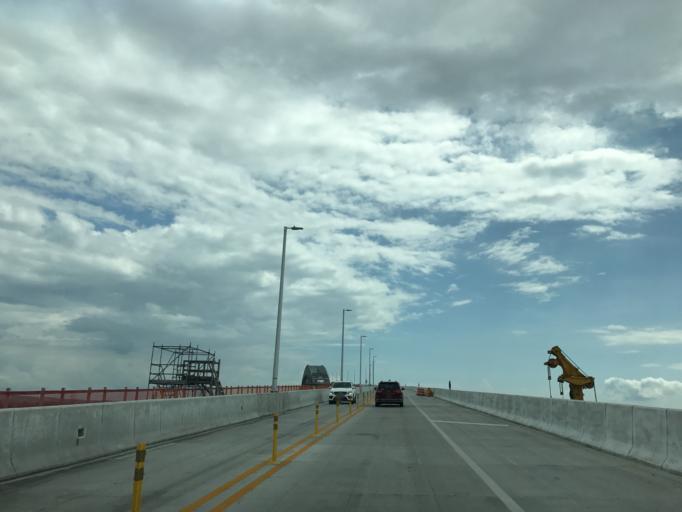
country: US
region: New Jersey
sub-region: Hudson County
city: Bayonne
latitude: 40.6500
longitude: -74.1382
